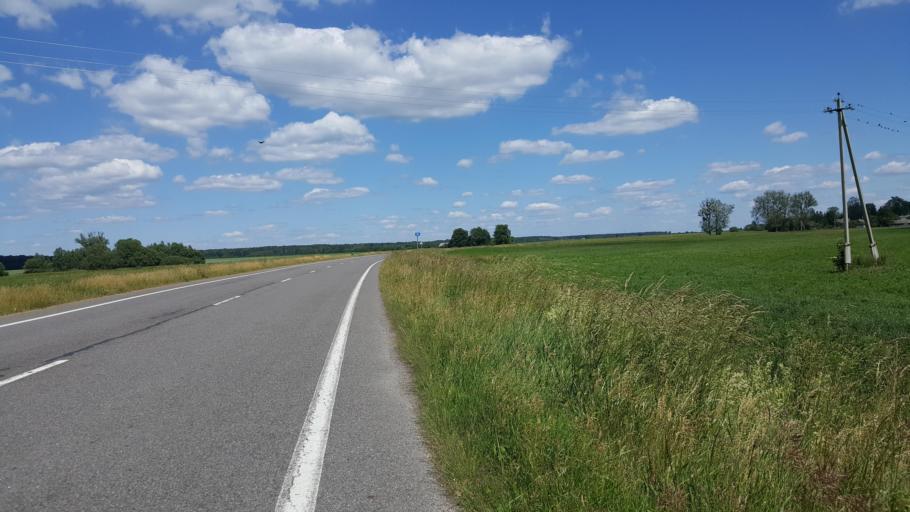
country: PL
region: Podlasie
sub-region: Powiat hajnowski
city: Czeremcha
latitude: 52.5019
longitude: 23.4987
